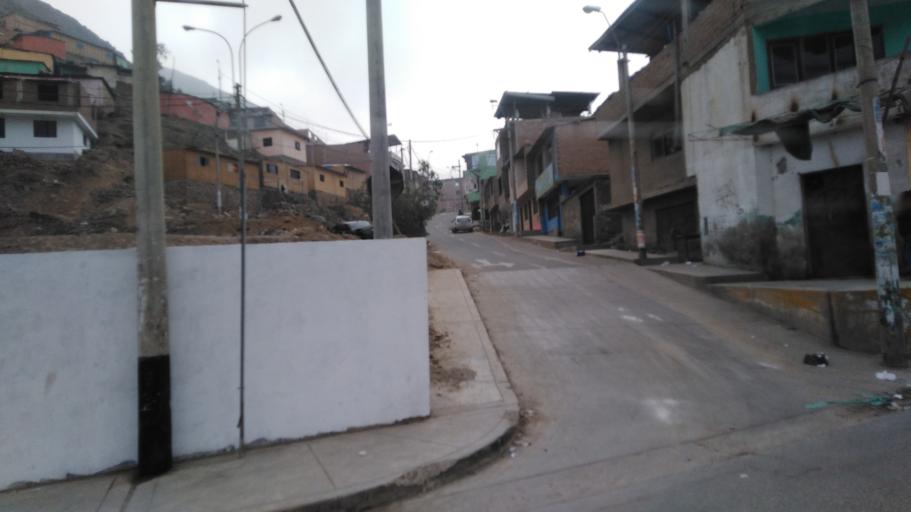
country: PE
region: Lima
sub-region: Lima
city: La Molina
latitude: -12.1448
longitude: -76.9375
